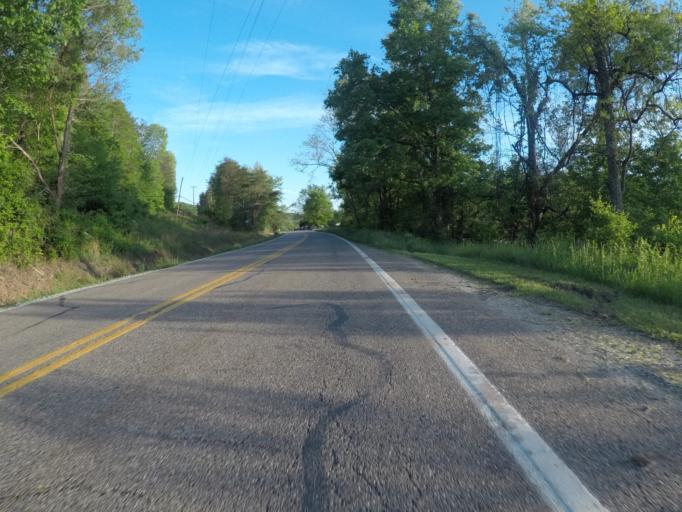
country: US
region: West Virginia
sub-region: Cabell County
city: Huntington
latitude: 38.5058
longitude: -82.4777
